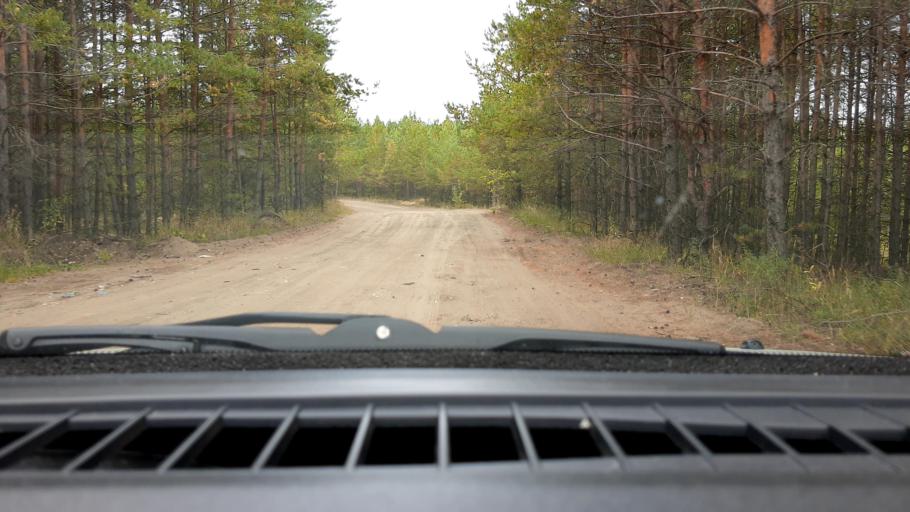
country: RU
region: Nizjnij Novgorod
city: Gorbatovka
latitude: 56.3192
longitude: 43.6954
